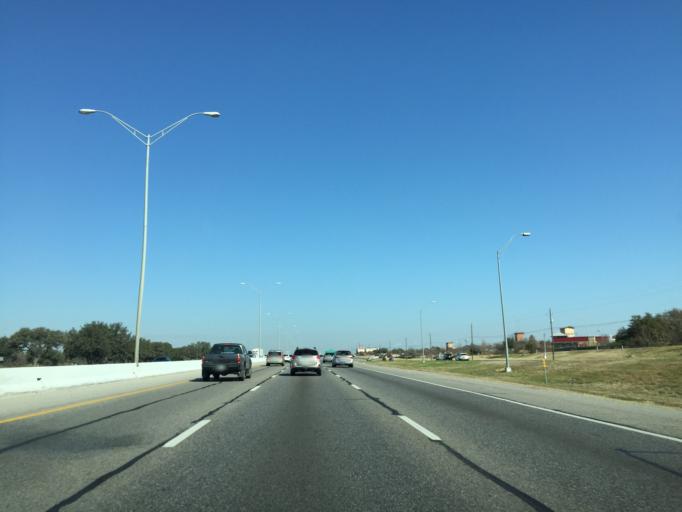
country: US
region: Texas
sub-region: Williamson County
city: Round Rock
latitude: 30.5610
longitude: -97.6926
